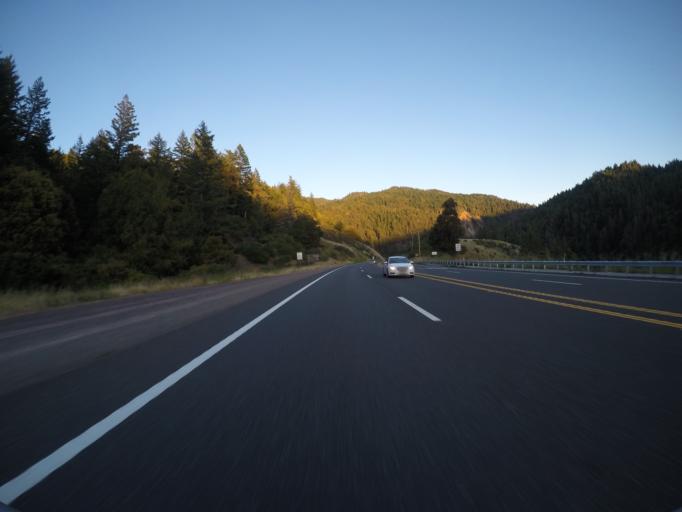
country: US
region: California
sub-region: Humboldt County
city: Redway
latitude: 39.9320
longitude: -123.7651
